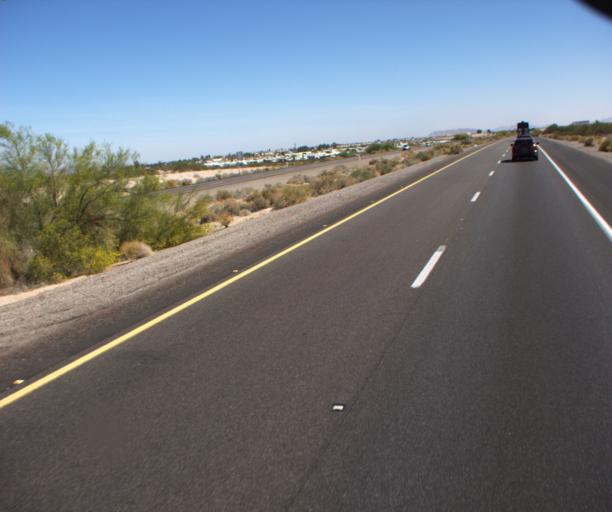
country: US
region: Arizona
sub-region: Yuma County
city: Wellton
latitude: 32.6587
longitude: -114.1547
